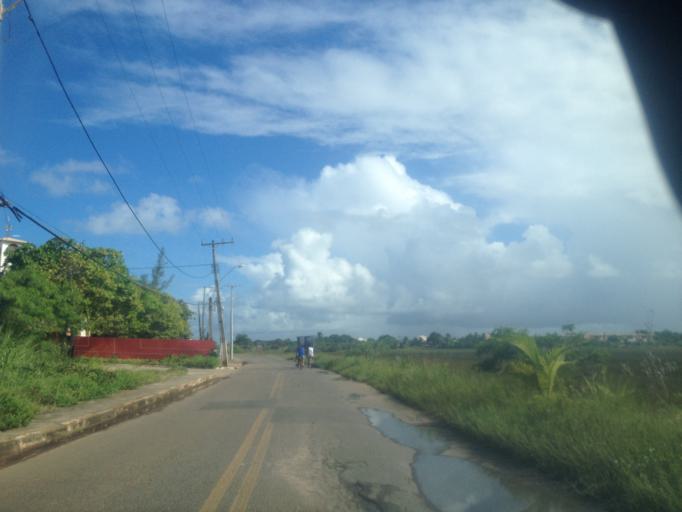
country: BR
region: Bahia
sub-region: Mata De Sao Joao
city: Mata de Sao Joao
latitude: -12.6205
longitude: -38.0471
